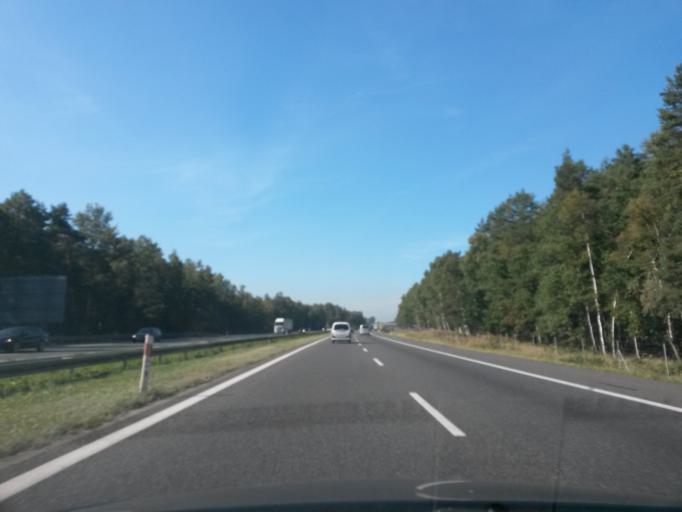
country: PL
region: Lesser Poland Voivodeship
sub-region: Powiat chrzanowski
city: Regulice
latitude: 50.1062
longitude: 19.5222
